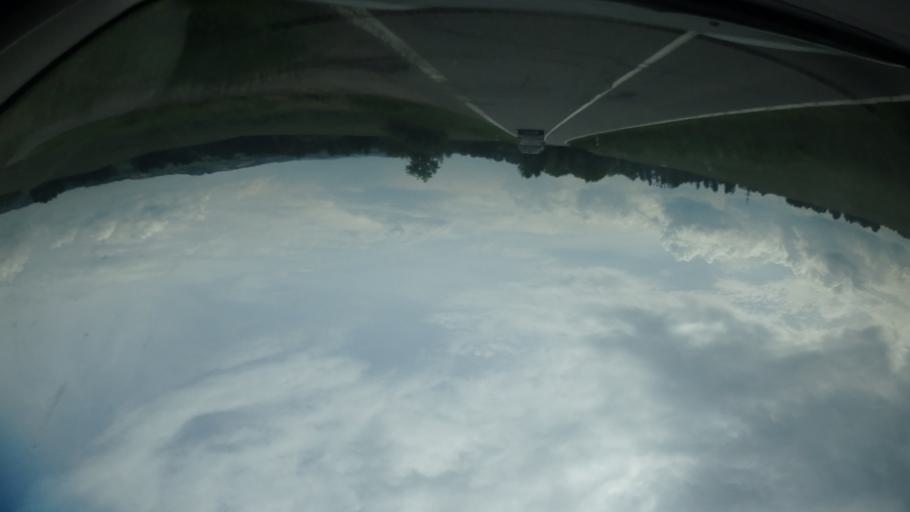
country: CZ
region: Vysocina
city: Bystrice nad Pernstejnem
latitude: 49.5180
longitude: 16.2920
